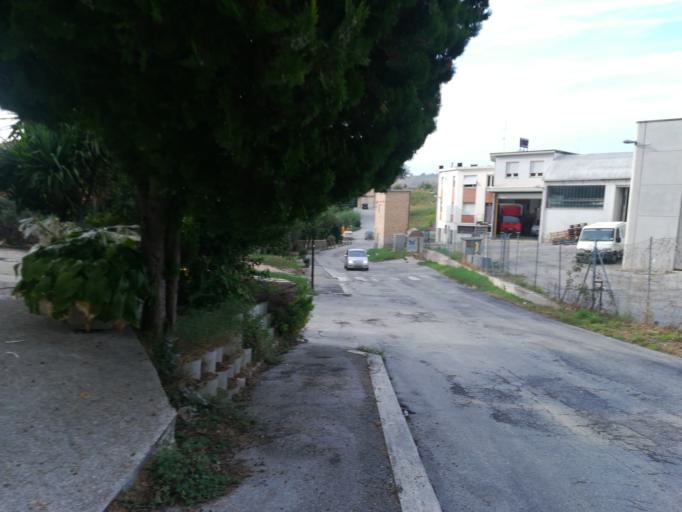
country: IT
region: The Marches
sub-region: Provincia di Macerata
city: Macerata
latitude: 43.3103
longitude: 13.4632
